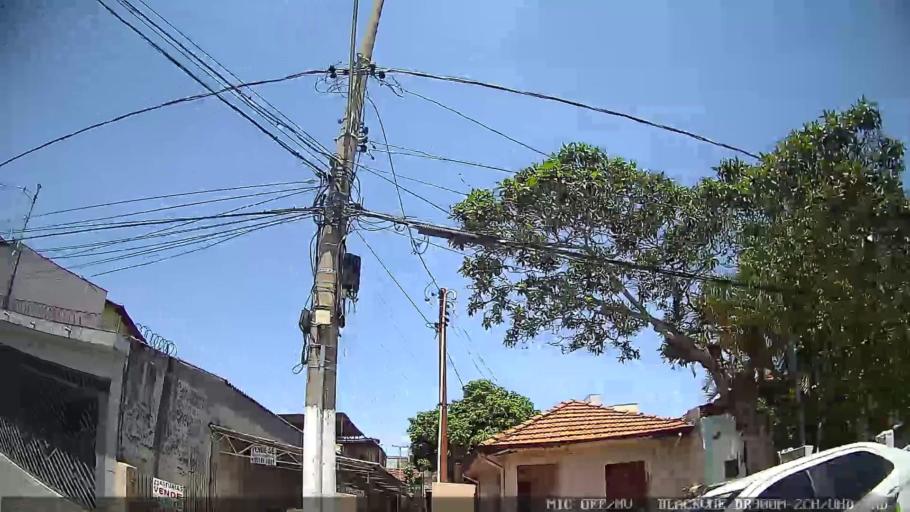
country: BR
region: Sao Paulo
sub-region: Guarulhos
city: Guarulhos
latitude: -23.5190
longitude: -46.5506
